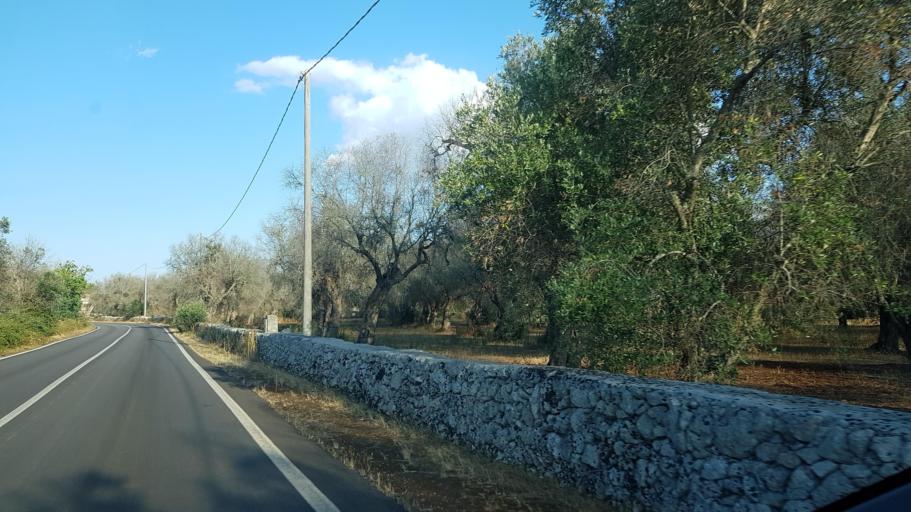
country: IT
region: Apulia
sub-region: Provincia di Lecce
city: Andrano
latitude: 39.9820
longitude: 18.3685
